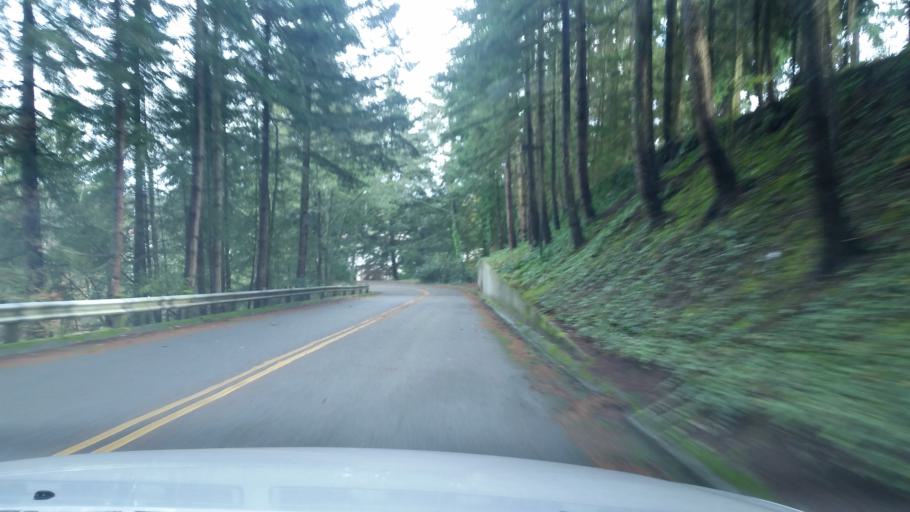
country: US
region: Washington
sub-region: King County
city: Shoreline
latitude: 47.7416
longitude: -122.3524
